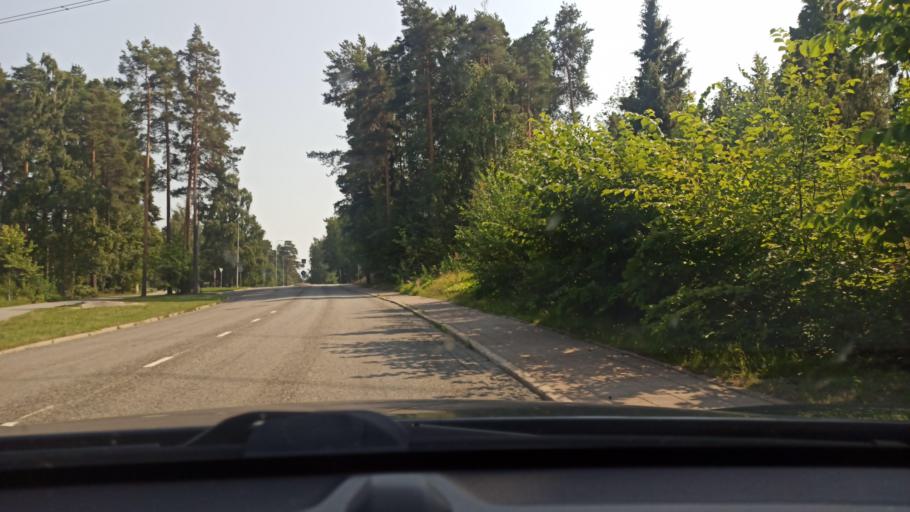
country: FI
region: Varsinais-Suomi
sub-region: Turku
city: Raisio
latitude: 60.4639
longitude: 22.2165
